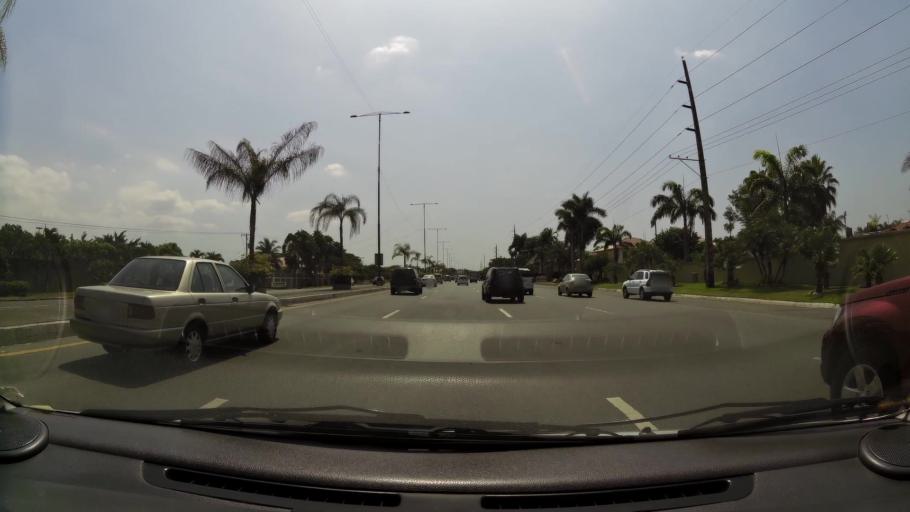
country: EC
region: Guayas
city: Eloy Alfaro
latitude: -2.1053
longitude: -79.8727
